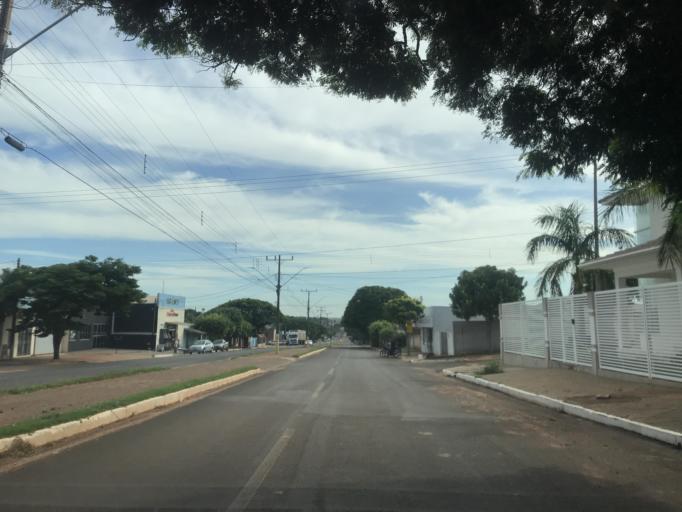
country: BR
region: Parana
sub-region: Paranavai
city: Nova Aurora
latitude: -22.9439
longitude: -52.6923
